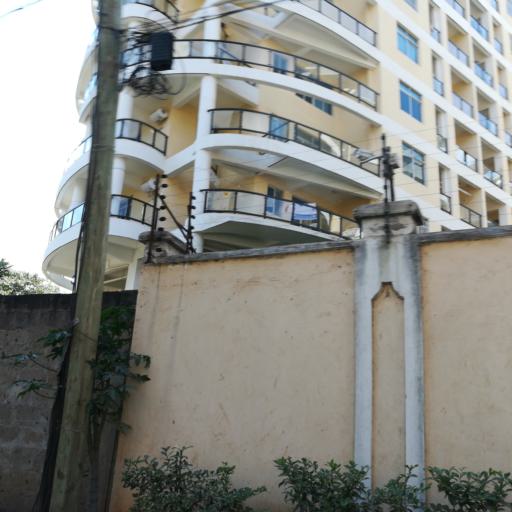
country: KE
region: Nairobi Area
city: Nairobi
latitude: -1.2958
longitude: 36.7927
